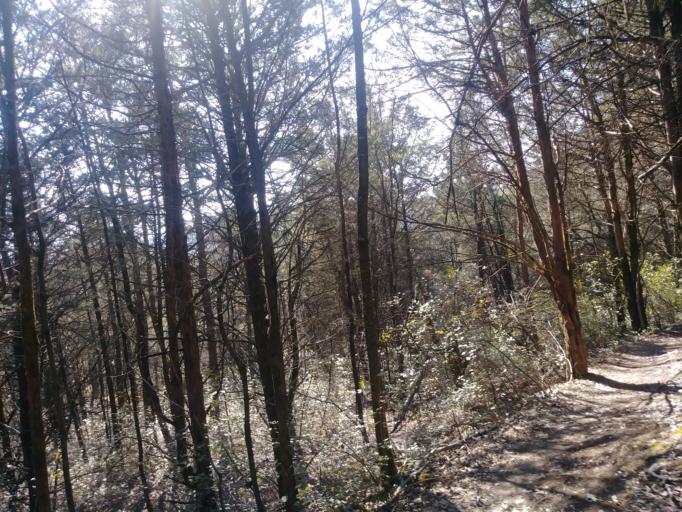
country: US
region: Tennessee
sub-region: Greene County
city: Greeneville
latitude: 36.1531
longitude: -82.8410
